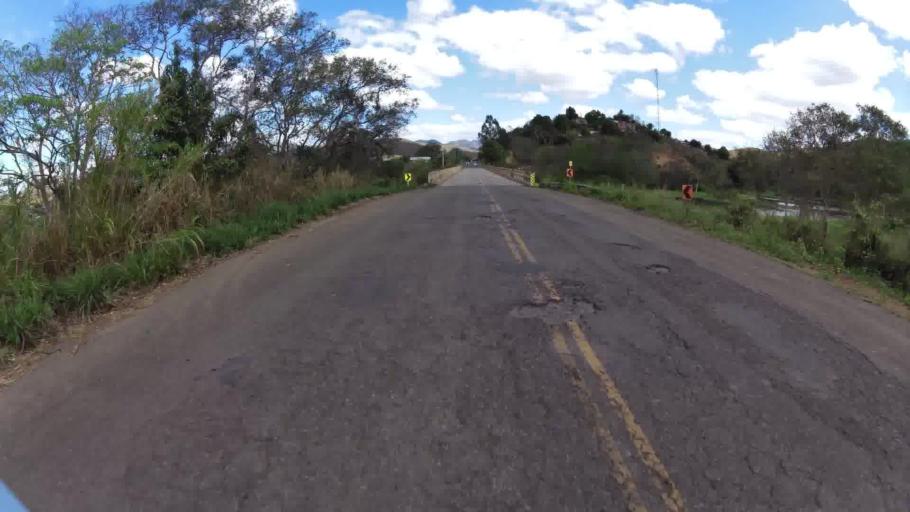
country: BR
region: Rio de Janeiro
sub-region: Itaperuna
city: Itaperuna
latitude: -21.2727
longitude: -41.7830
